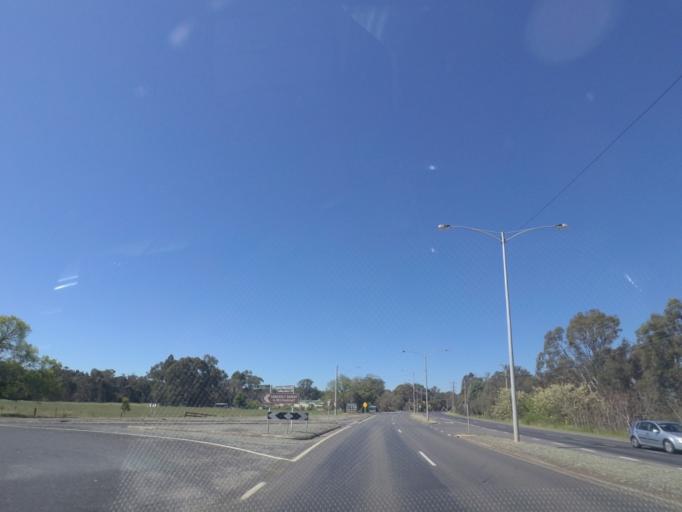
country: AU
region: Victoria
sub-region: Murrindindi
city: Kinglake West
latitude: -37.0225
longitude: 145.1158
